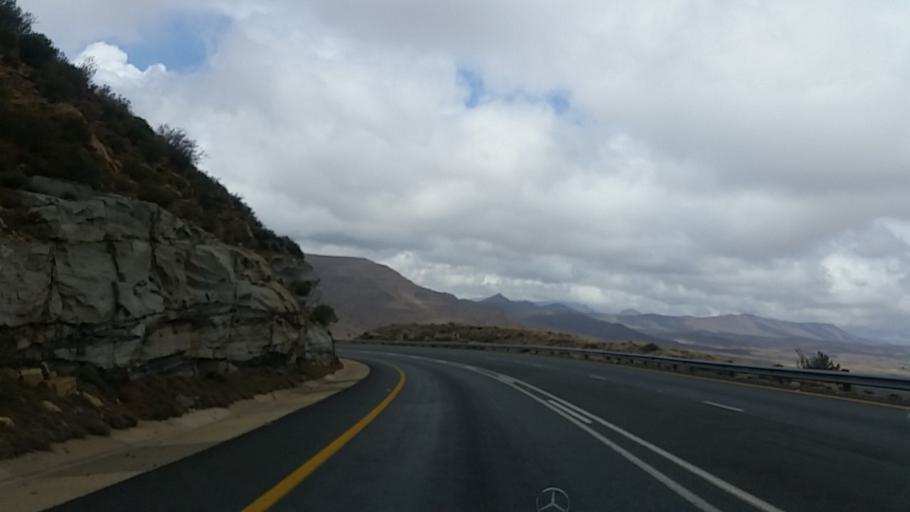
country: ZA
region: Eastern Cape
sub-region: Chris Hani District Municipality
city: Middelburg
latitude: -31.8405
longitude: 24.8663
